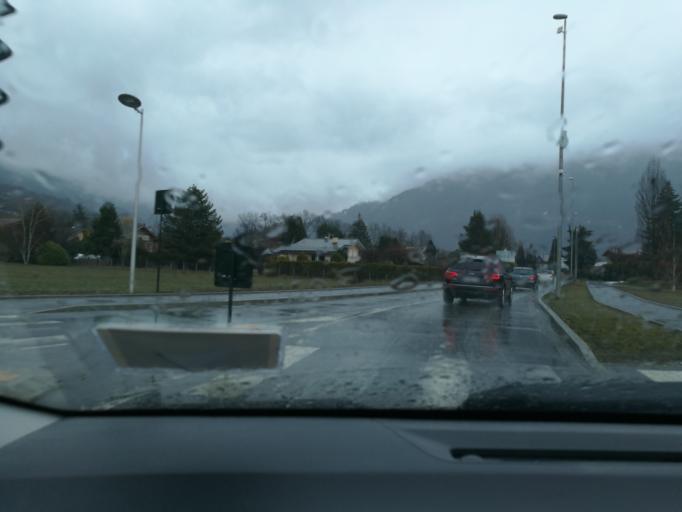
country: FR
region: Rhone-Alpes
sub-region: Departement de la Haute-Savoie
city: Passy
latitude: 45.9167
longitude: 6.6943
